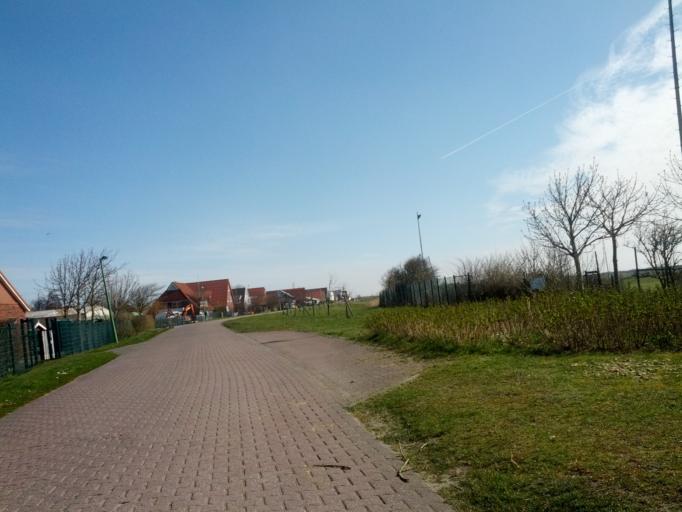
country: DE
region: Lower Saxony
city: Langeoog
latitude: 53.7445
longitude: 7.4893
